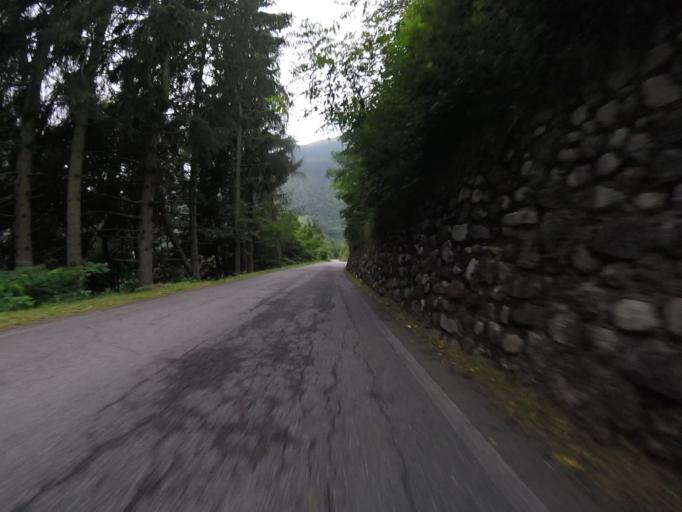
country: IT
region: Lombardy
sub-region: Provincia di Brescia
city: Monno
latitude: 46.2168
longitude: 10.3310
